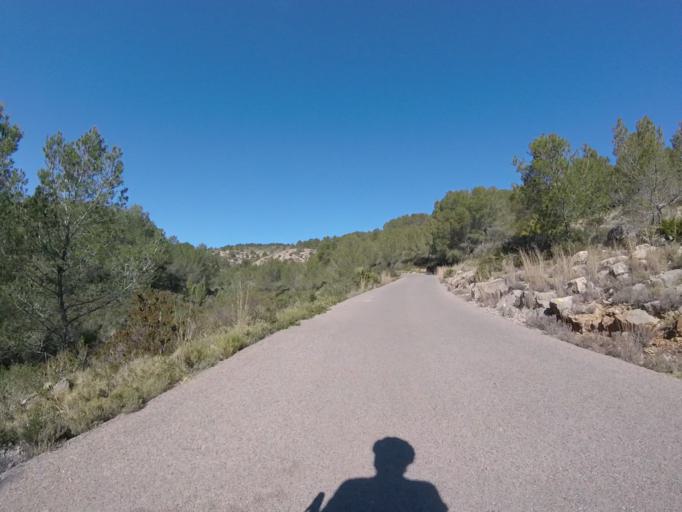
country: ES
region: Valencia
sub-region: Provincia de Castello
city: Benicassim
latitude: 40.0775
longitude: 0.0929
